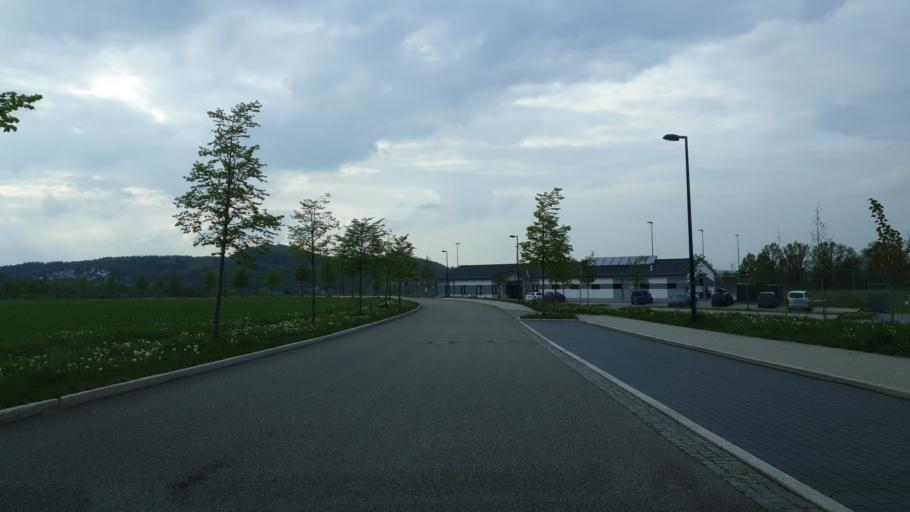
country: DE
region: Saxony
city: Oelsnitz
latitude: 50.7170
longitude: 12.7138
